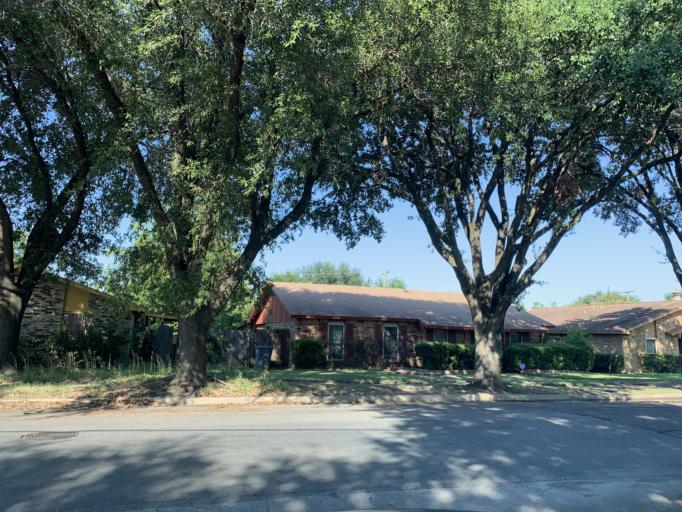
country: US
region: Texas
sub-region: Dallas County
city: Hutchins
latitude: 32.6613
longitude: -96.7730
